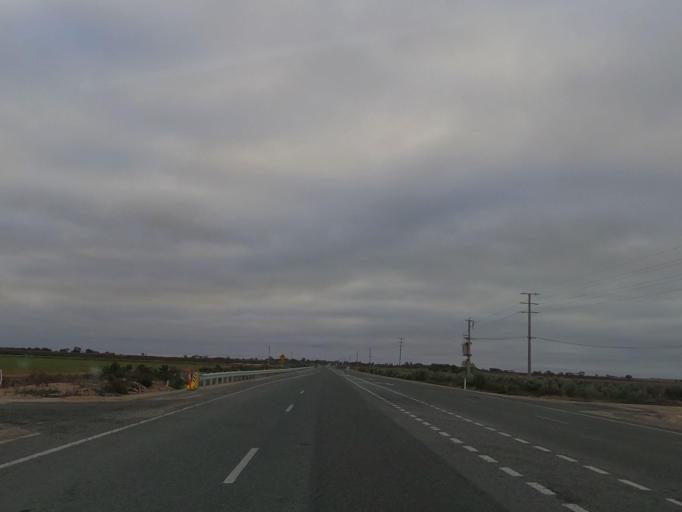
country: AU
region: Victoria
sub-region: Swan Hill
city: Swan Hill
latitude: -35.4754
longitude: 143.6786
